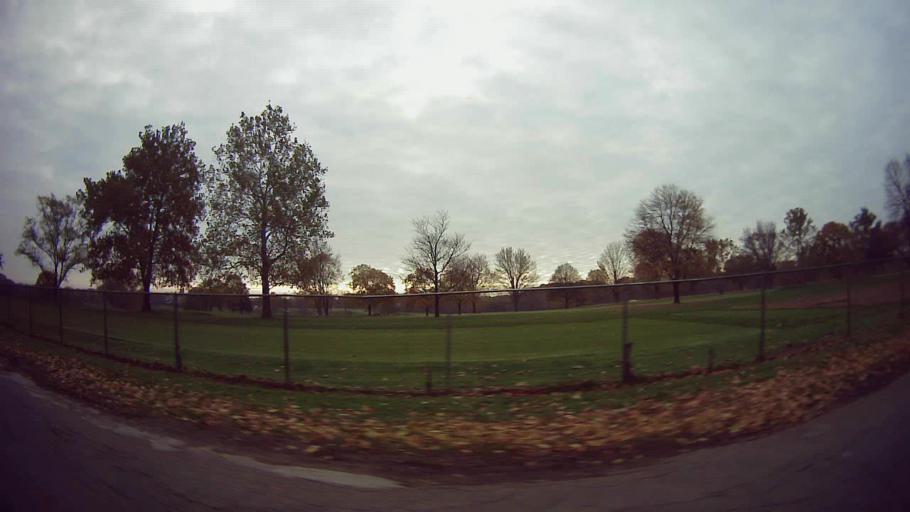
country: US
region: Michigan
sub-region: Oakland County
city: Beverly Hills
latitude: 42.5346
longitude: -83.2426
